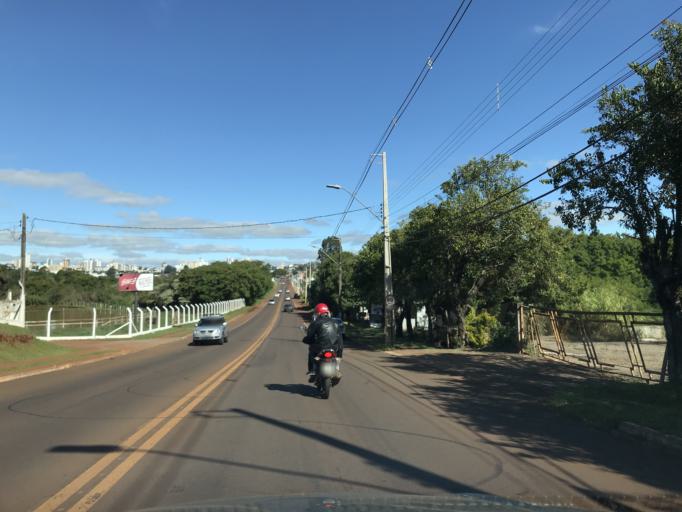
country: BR
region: Parana
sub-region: Cascavel
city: Cascavel
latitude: -24.9248
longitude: -53.4746
